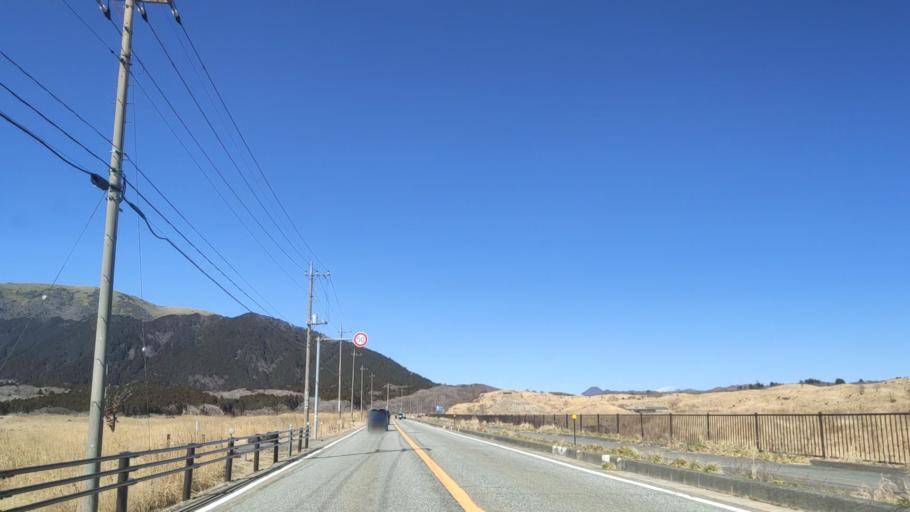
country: JP
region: Yamanashi
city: Fujikawaguchiko
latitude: 35.4191
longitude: 138.5911
